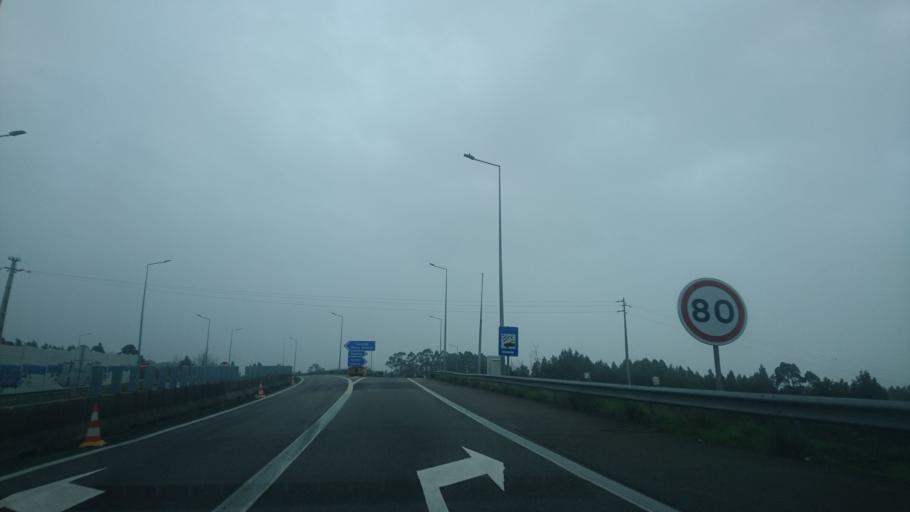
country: PT
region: Porto
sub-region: Vila Nova de Gaia
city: Gulpilhares
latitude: 41.0824
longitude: -8.6313
